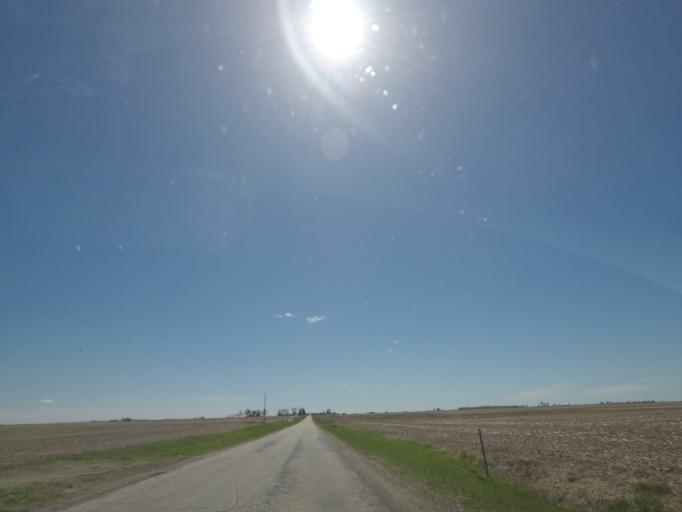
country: US
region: Illinois
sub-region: Logan County
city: Atlanta
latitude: 40.1791
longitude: -89.1939
